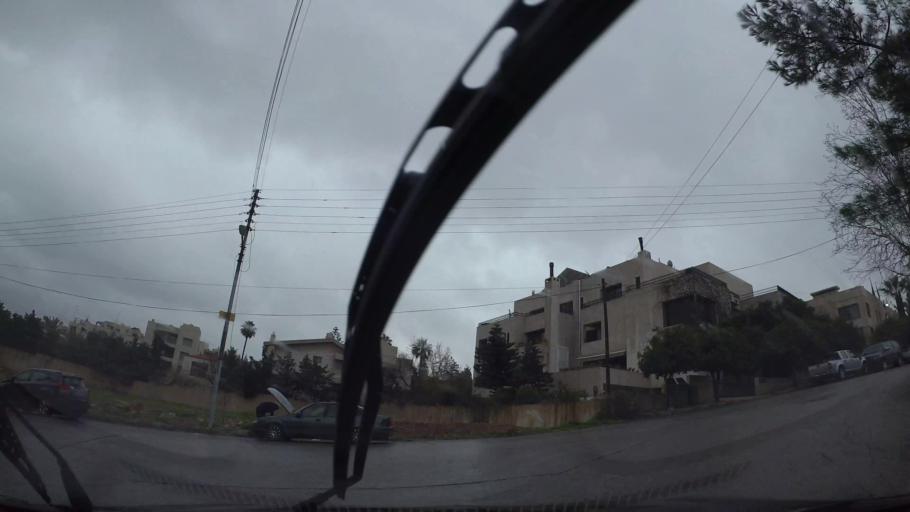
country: JO
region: Amman
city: Amman
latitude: 31.9581
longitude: 35.8981
